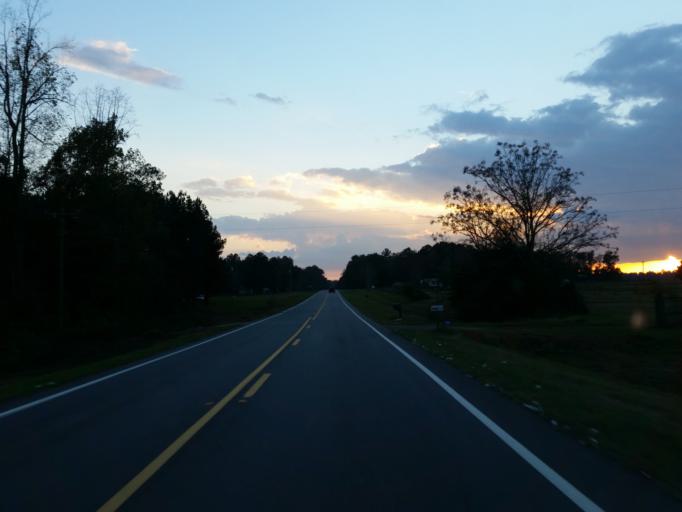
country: US
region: Georgia
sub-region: Pulaski County
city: Hawkinsville
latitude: 32.2266
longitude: -83.5175
